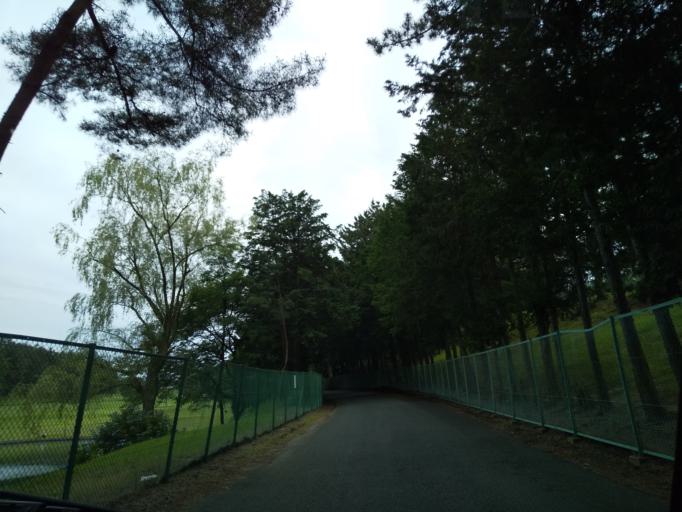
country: JP
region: Kanagawa
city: Atsugi
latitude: 35.4789
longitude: 139.3253
